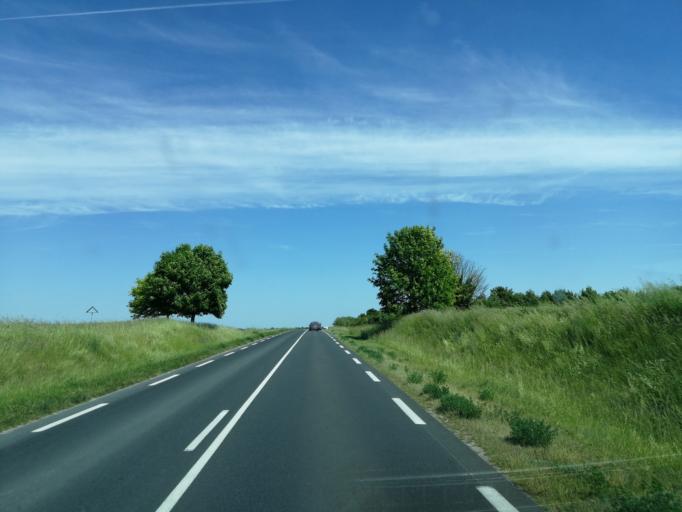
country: FR
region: Poitou-Charentes
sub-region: Departement de la Vienne
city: Loudun
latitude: 47.0237
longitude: 0.0882
